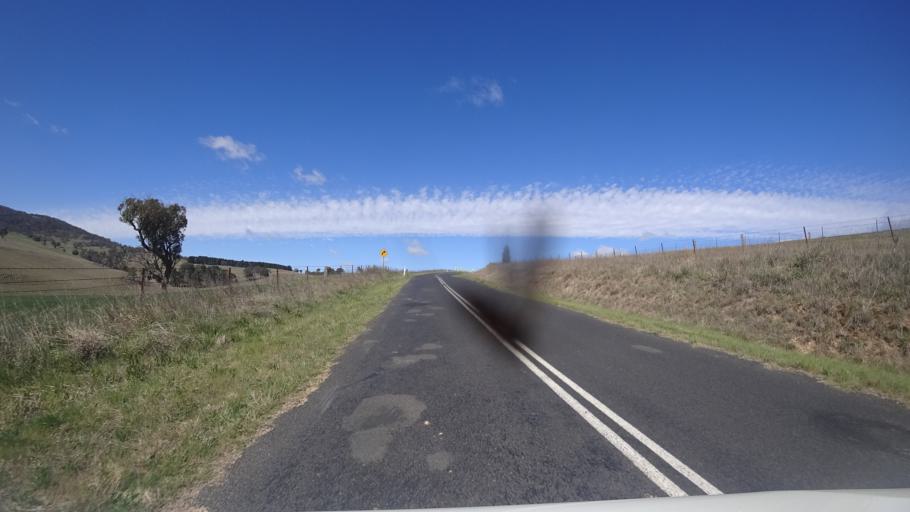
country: AU
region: New South Wales
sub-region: Lithgow
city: Portland
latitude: -33.5180
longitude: 149.9524
